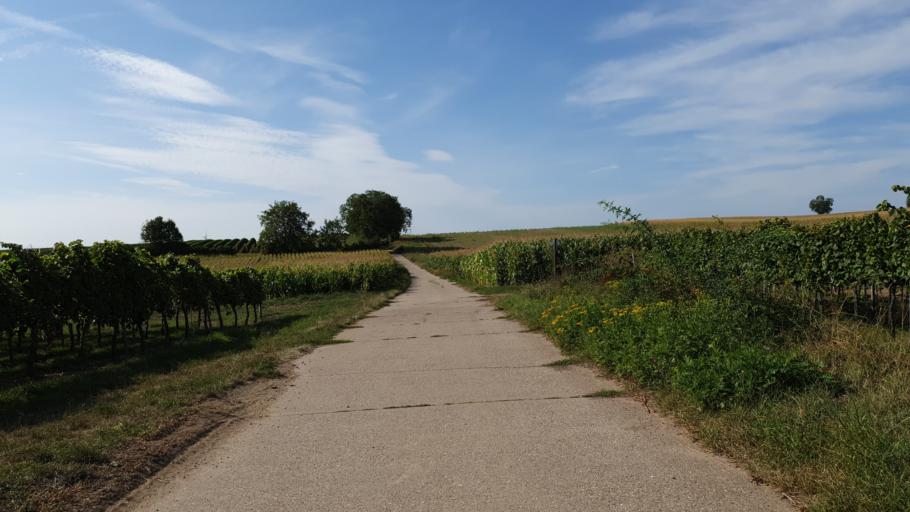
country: DE
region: Rheinland-Pfalz
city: Billigheim-Ingenheim
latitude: 49.1169
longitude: 8.1011
